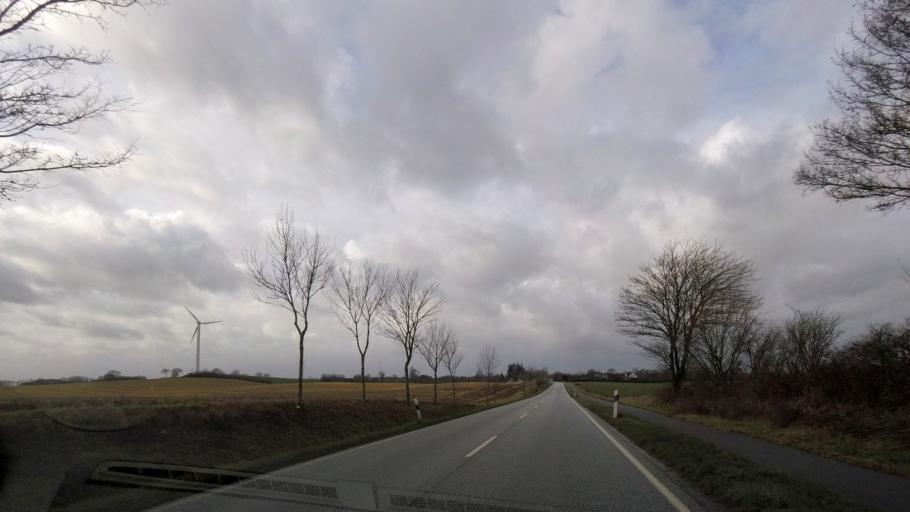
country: DE
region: Schleswig-Holstein
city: Dollrottfeld
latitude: 54.6436
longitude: 9.8264
